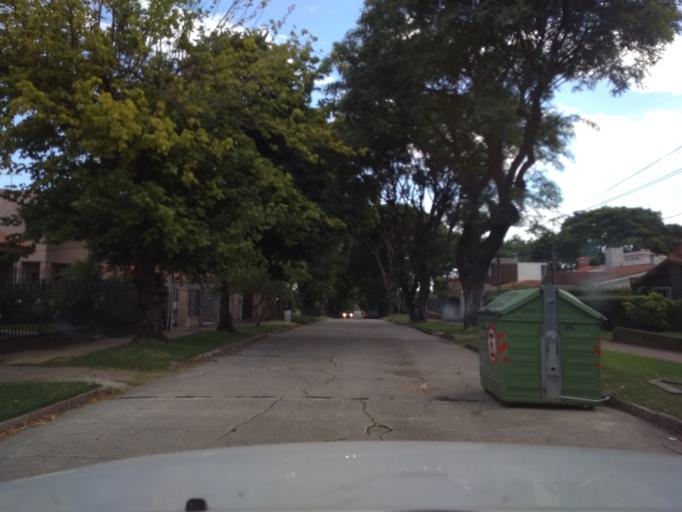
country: UY
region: Canelones
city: Paso de Carrasco
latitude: -34.8893
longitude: -56.0845
